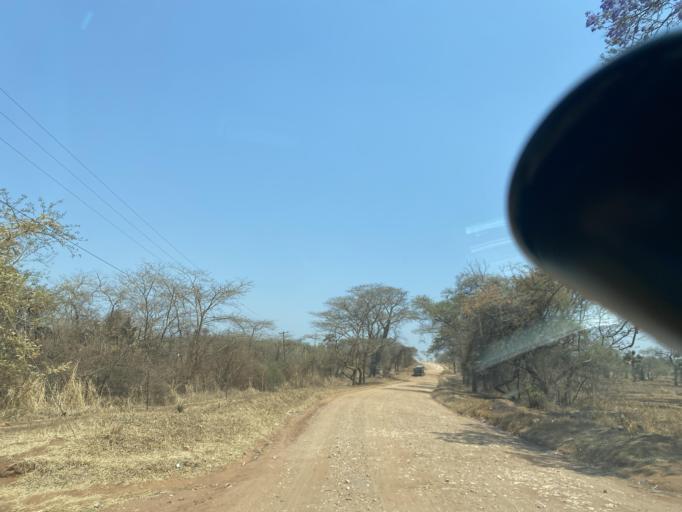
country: ZM
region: Lusaka
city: Kafue
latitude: -15.5490
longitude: 28.0655
